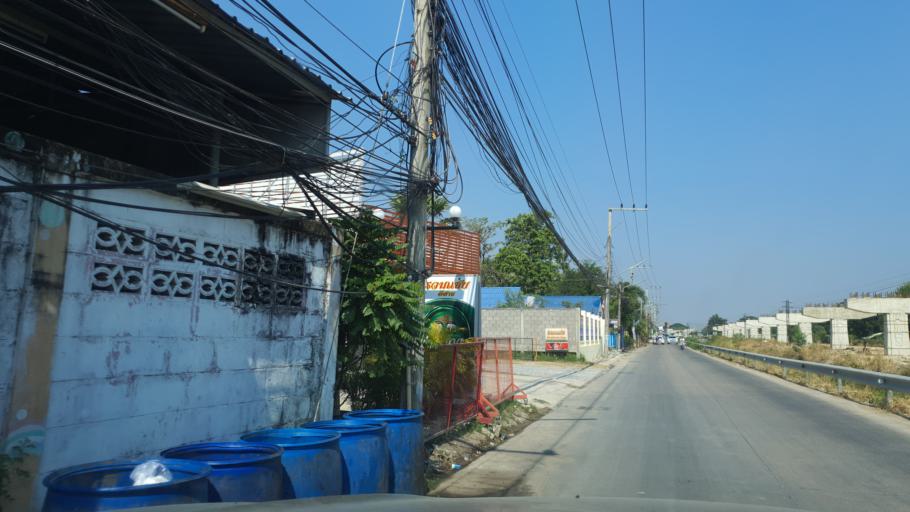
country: TH
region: Prachuap Khiri Khan
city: Hua Hin
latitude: 12.5579
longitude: 99.9567
